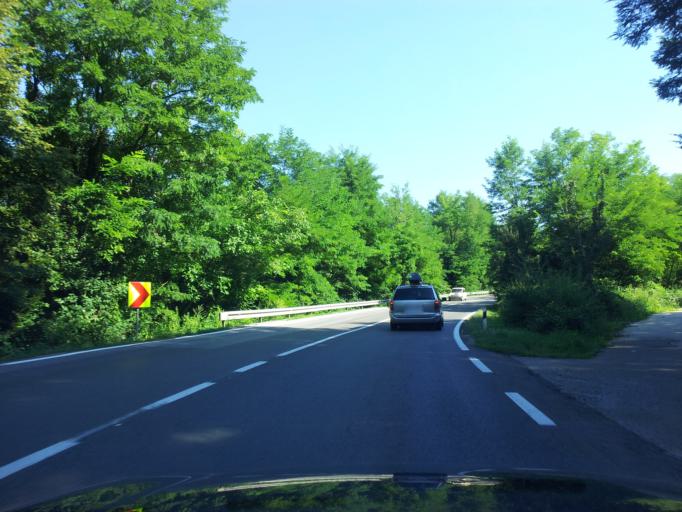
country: HR
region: Karlovacka
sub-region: Grad Karlovac
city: Slunj
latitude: 45.2485
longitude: 15.5508
